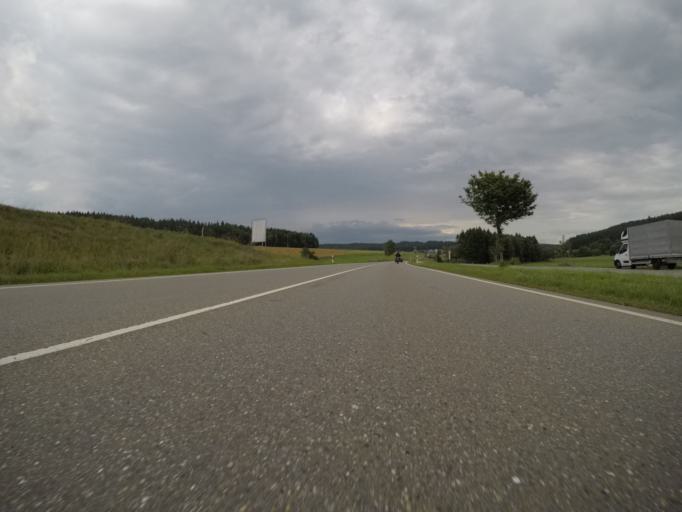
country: DE
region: Baden-Wuerttemberg
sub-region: Freiburg Region
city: Sankt Georgen im Schwarzwald
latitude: 48.1310
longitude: 8.3602
